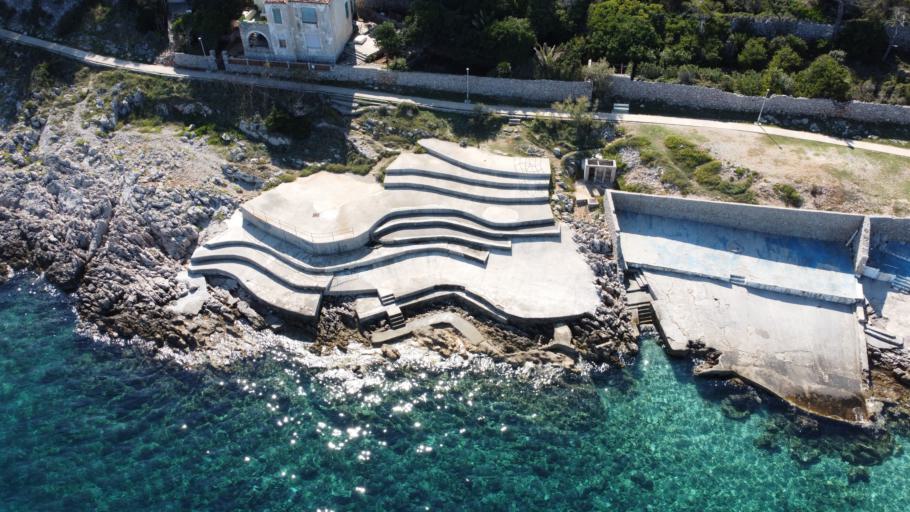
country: HR
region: Primorsko-Goranska
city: Mali Losinj
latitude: 44.5237
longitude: 14.5036
